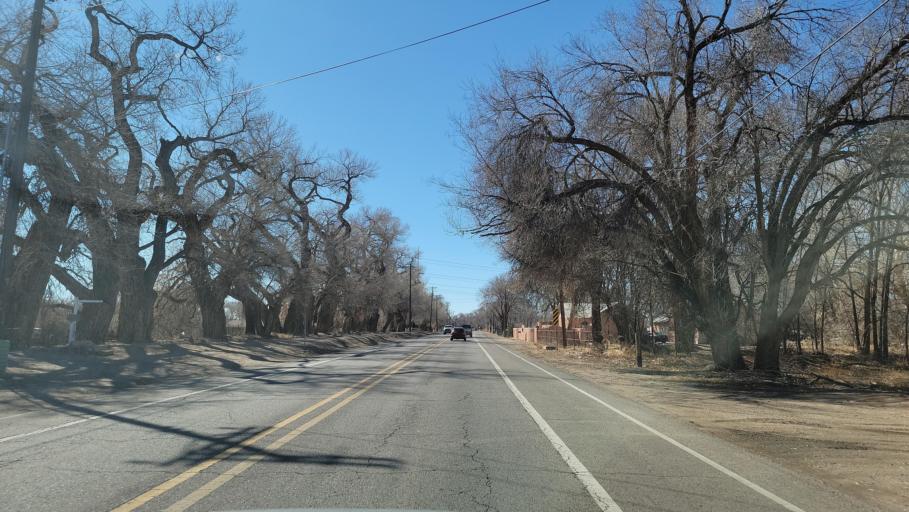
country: US
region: New Mexico
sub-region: Bernalillo County
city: South Valley
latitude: 35.0073
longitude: -106.6888
